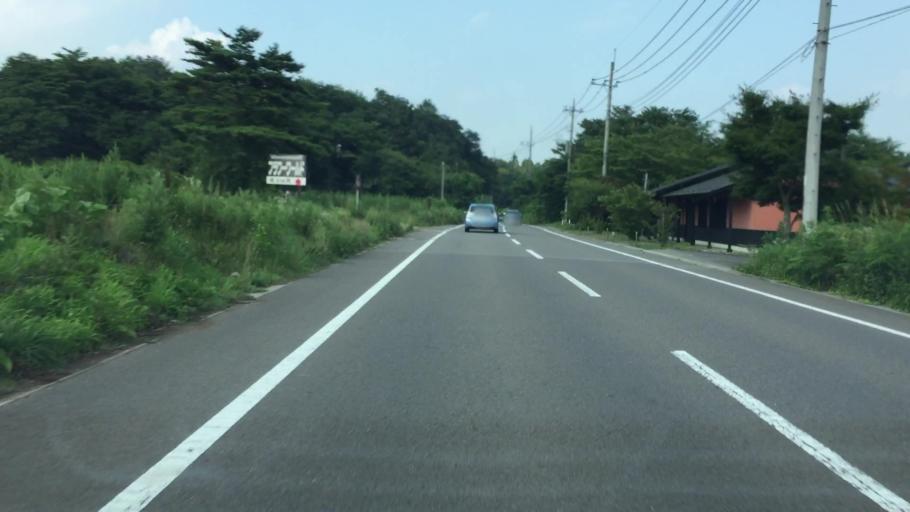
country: JP
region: Tochigi
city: Kuroiso
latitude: 37.0826
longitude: 140.0540
